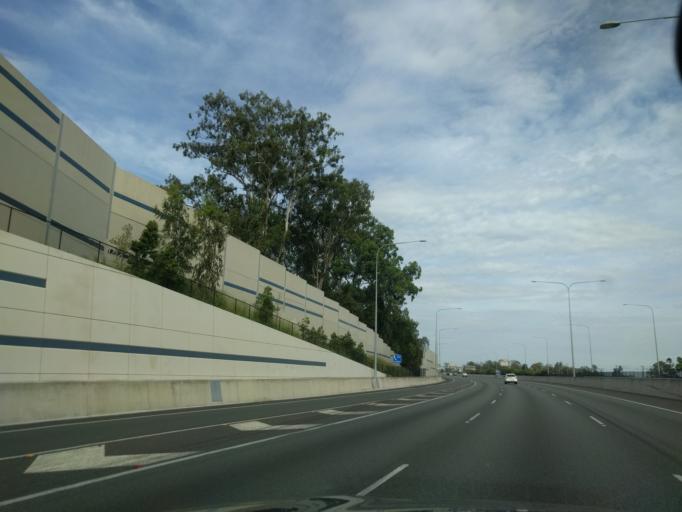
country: AU
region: Queensland
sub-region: Ipswich
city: Goodna
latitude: -27.6054
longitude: 152.8942
